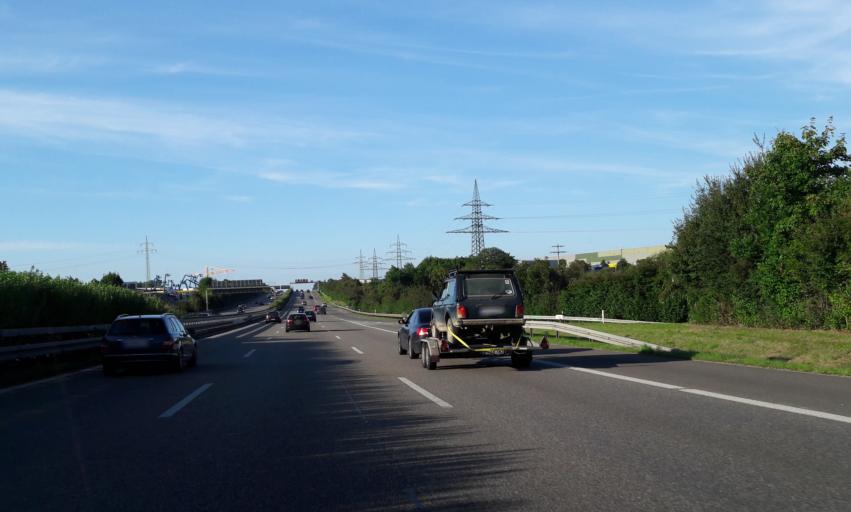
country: DE
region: Baden-Wuerttemberg
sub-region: Regierungsbezirk Stuttgart
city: Moglingen
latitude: 48.8836
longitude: 9.1450
